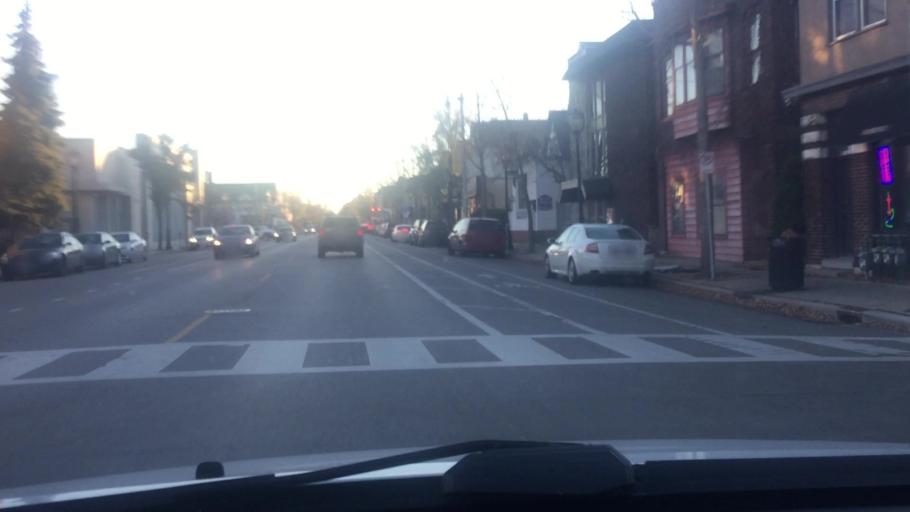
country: US
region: Wisconsin
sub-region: Milwaukee County
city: Shorewood
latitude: 43.0728
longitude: -87.8880
